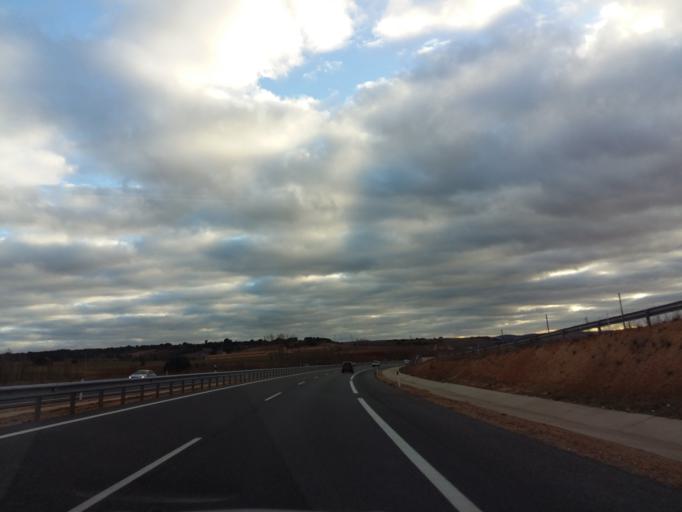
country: ES
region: Castille and Leon
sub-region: Provincia de Burgos
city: Villalmanzo
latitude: 42.0711
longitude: -3.7329
